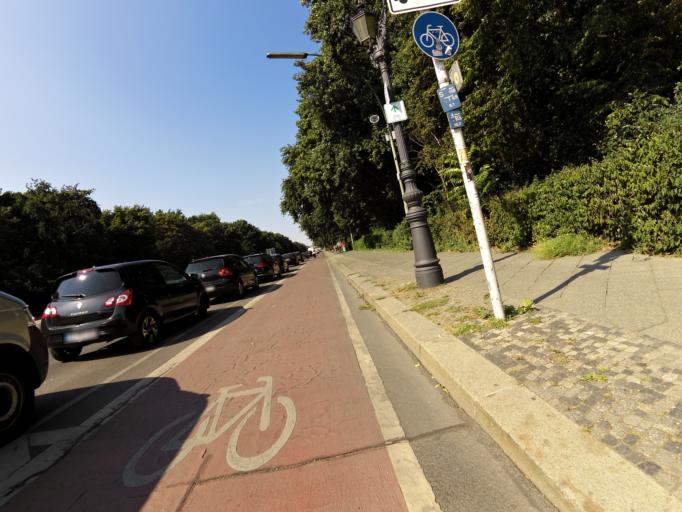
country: DE
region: Berlin
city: Hansaviertel
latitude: 52.5145
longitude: 13.3482
